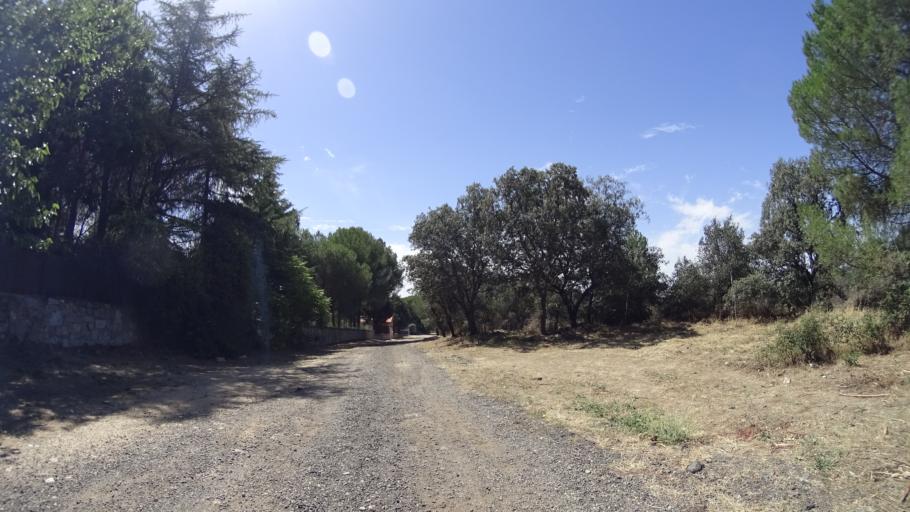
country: ES
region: Madrid
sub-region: Provincia de Madrid
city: Torrelodones
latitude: 40.5714
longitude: -3.9449
